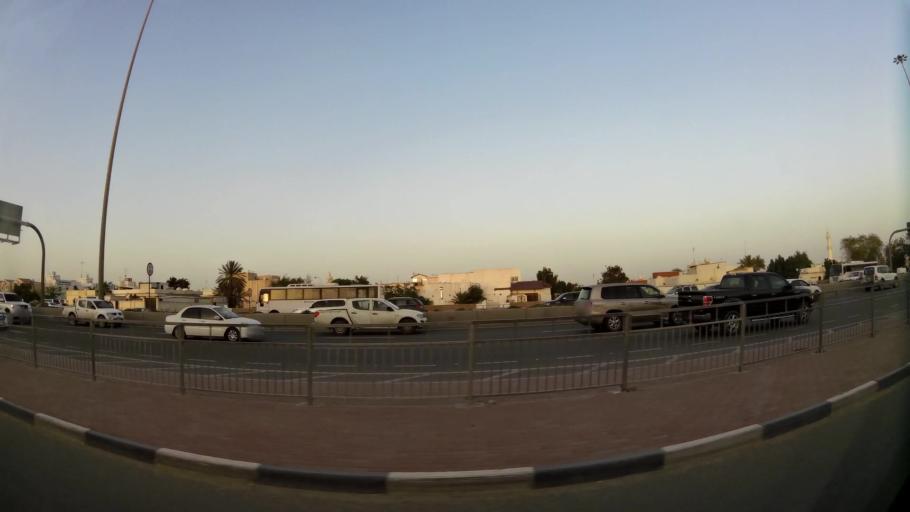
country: QA
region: Baladiyat ar Rayyan
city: Ar Rayyan
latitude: 25.3253
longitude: 51.4676
